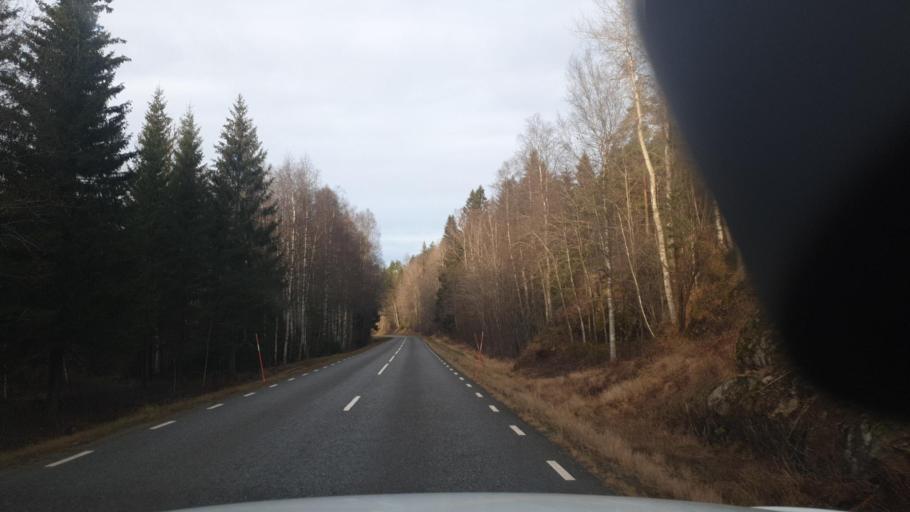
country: SE
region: Vaermland
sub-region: Eda Kommun
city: Amotfors
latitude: 59.6936
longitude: 12.0915
